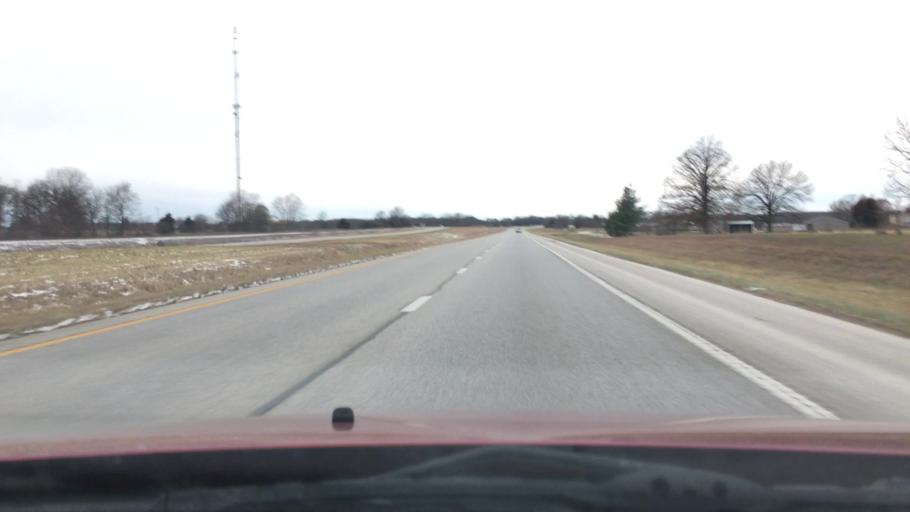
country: US
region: Missouri
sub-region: Webster County
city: Seymour
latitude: 37.1693
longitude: -92.8159
